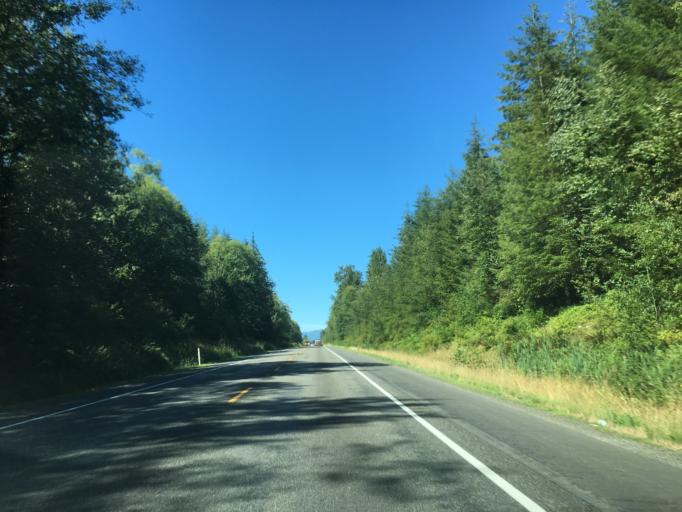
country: US
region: Washington
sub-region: Snohomish County
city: Sisco Heights
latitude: 48.1315
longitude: -122.1128
